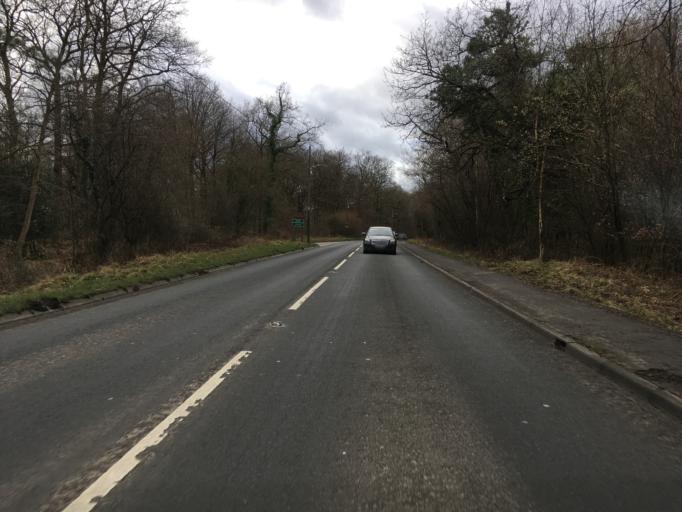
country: GB
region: England
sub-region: Gloucestershire
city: Cinderford
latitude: 51.8109
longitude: -2.5150
